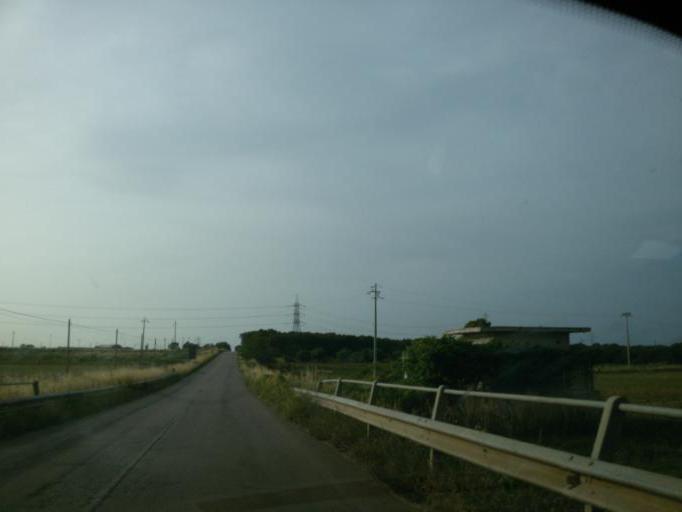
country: IT
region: Apulia
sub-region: Provincia di Brindisi
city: La Rosa
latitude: 40.5892
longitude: 17.9612
